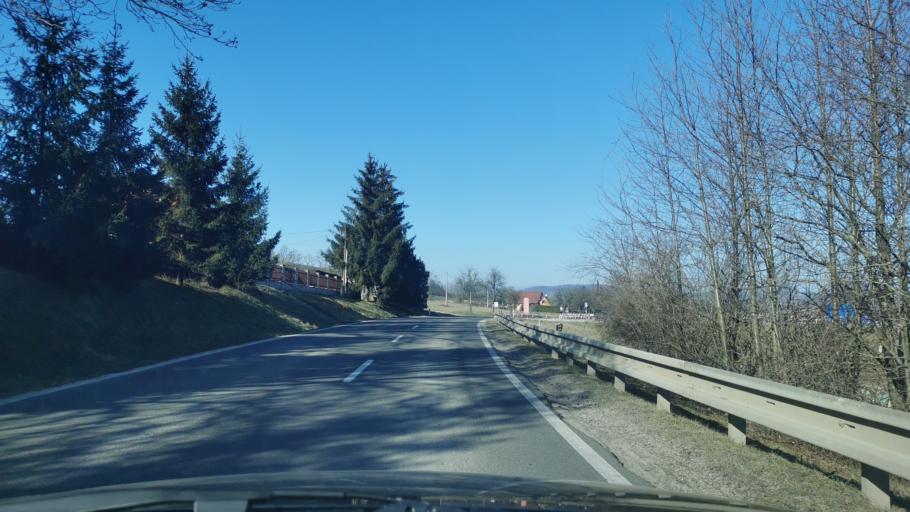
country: SK
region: Trnavsky
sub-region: Okres Senica
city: Senica
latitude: 48.7024
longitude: 17.4003
